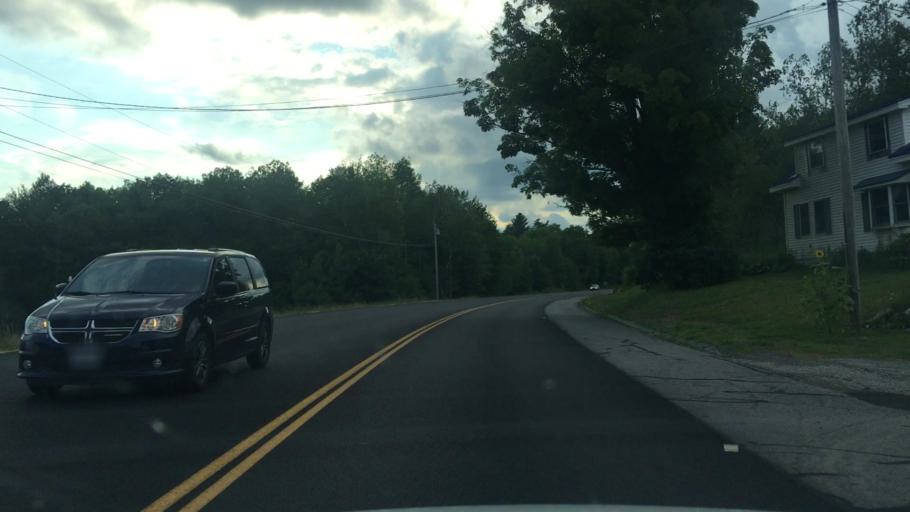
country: US
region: Maine
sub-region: Waldo County
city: Palermo
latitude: 44.3685
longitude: -69.3879
